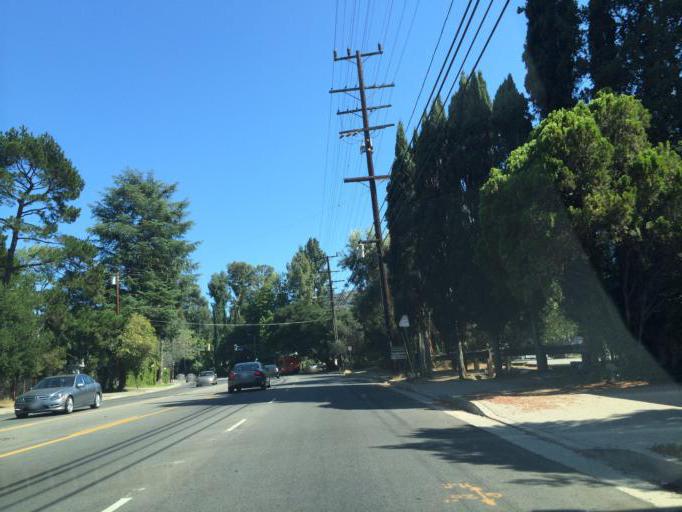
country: US
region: California
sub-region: Los Angeles County
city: Universal City
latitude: 34.1347
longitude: -118.3921
